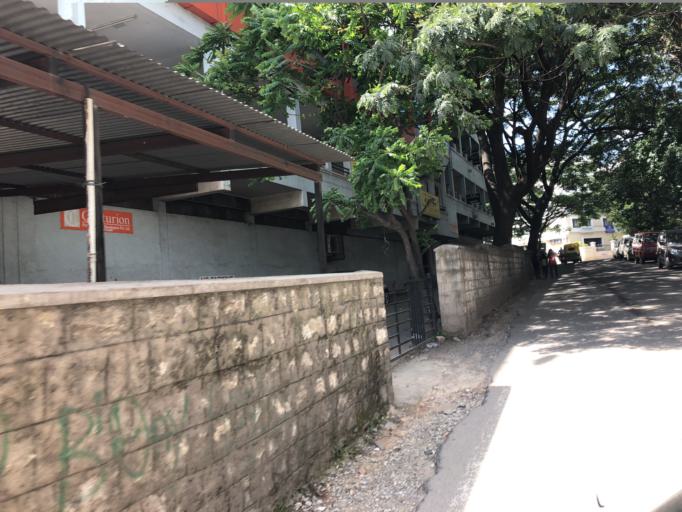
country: IN
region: Karnataka
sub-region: Bangalore Urban
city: Bangalore
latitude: 12.9623
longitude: 77.5876
